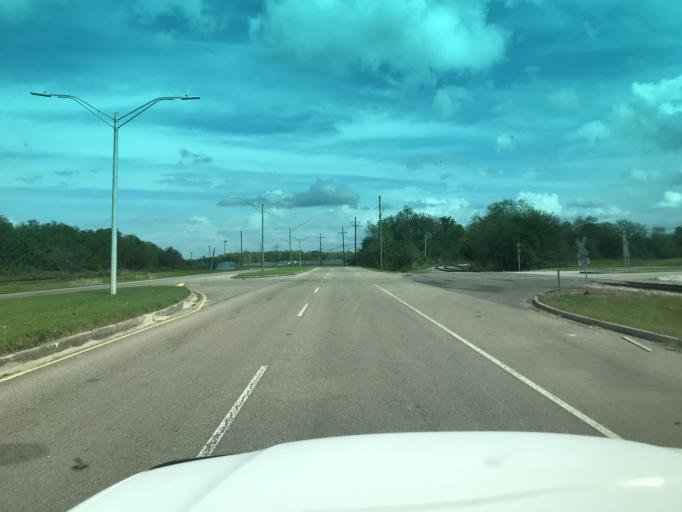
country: US
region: Louisiana
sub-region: Saint Bernard Parish
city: Arabi
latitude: 30.0042
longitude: -90.0153
